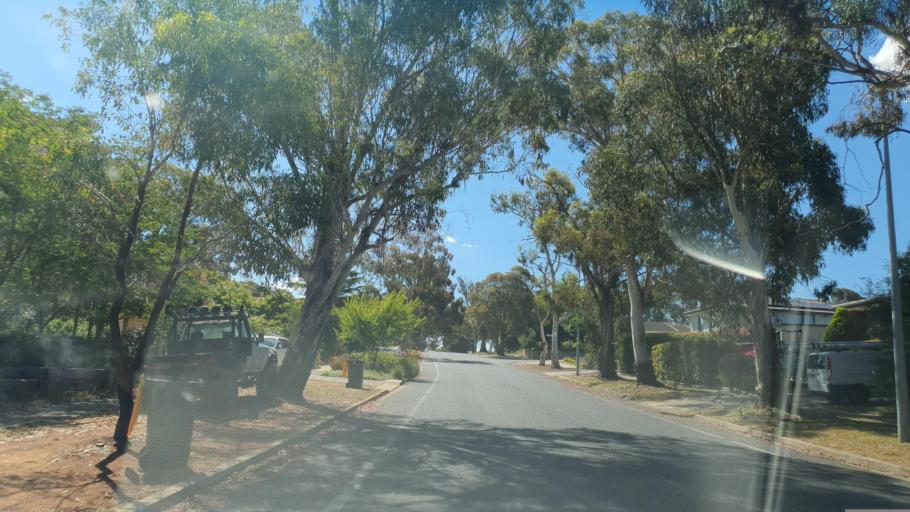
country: AU
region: Australian Capital Territory
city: Belconnen
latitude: -35.2132
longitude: 149.0453
